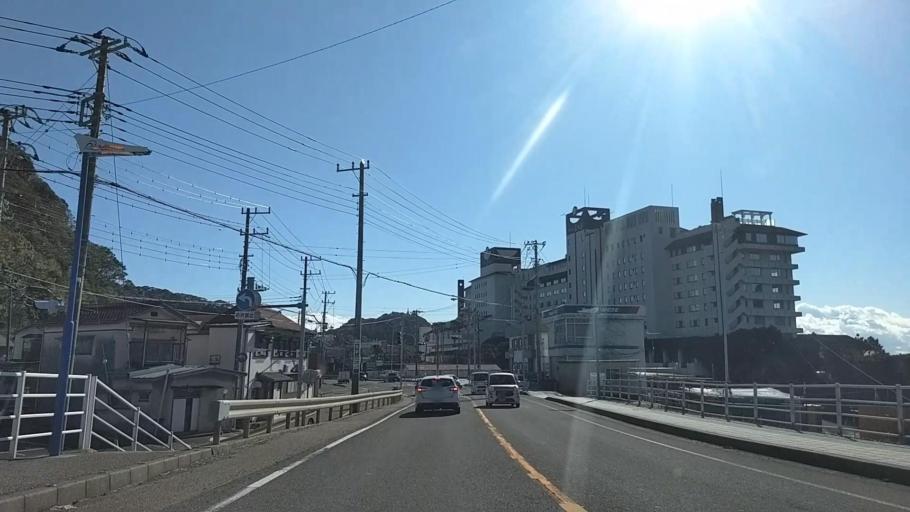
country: JP
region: Chiba
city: Kawaguchi
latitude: 35.1261
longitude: 140.1944
